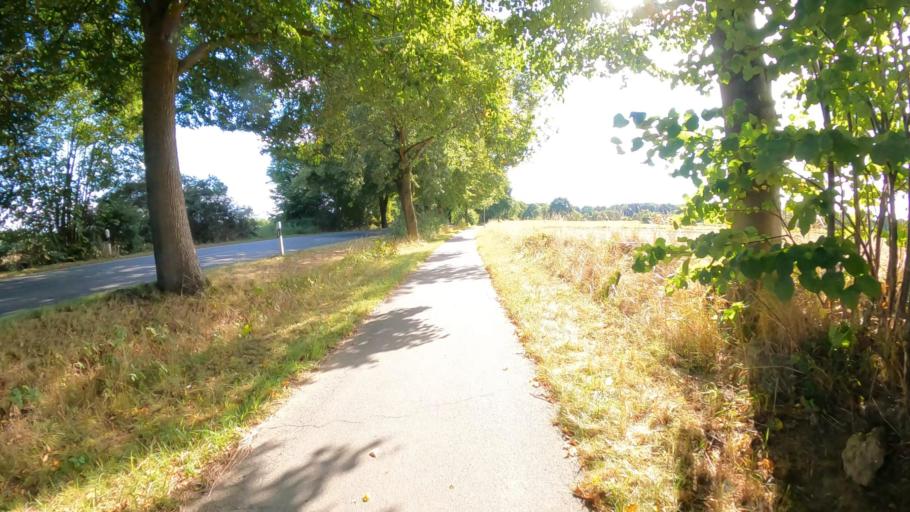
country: DE
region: Schleswig-Holstein
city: Hoisdorf
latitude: 53.6701
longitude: 10.3253
